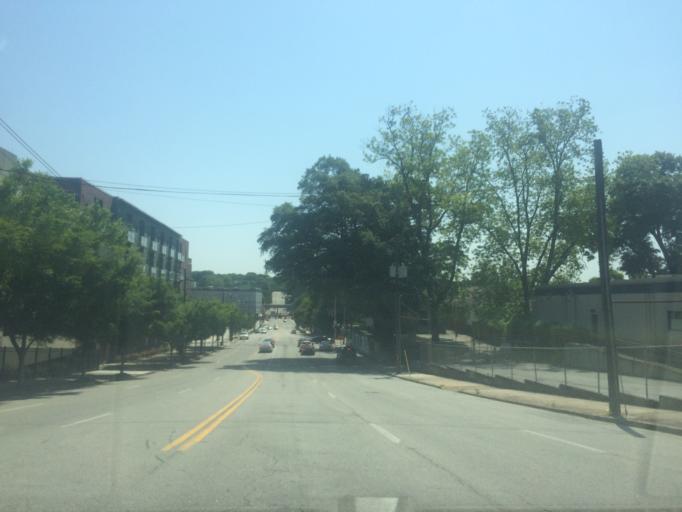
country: US
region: Georgia
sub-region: Fulton County
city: Atlanta
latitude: 33.7713
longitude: -84.3690
